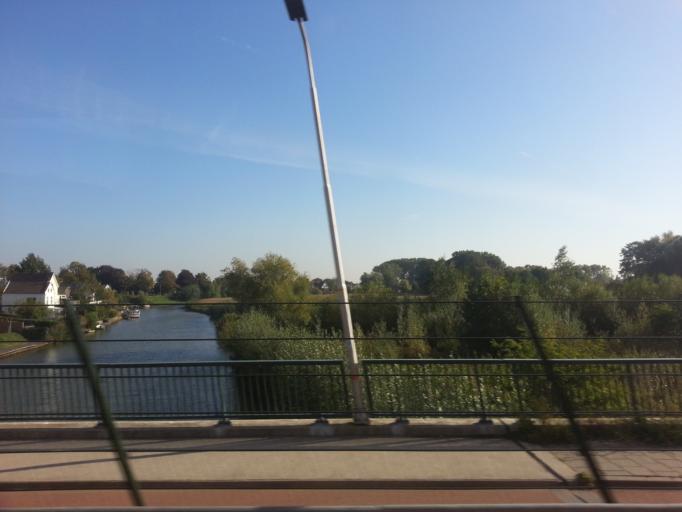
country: NL
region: Gelderland
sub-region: Gemeente Geldermalsen
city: Geldermalsen
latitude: 51.8876
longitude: 5.2693
